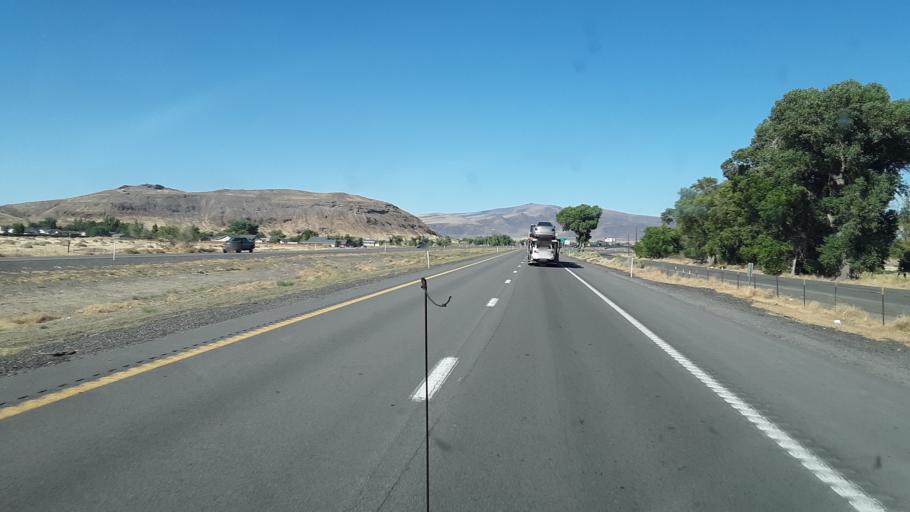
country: US
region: Nevada
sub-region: Lyon County
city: Fernley
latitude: 39.6116
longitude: -119.3159
